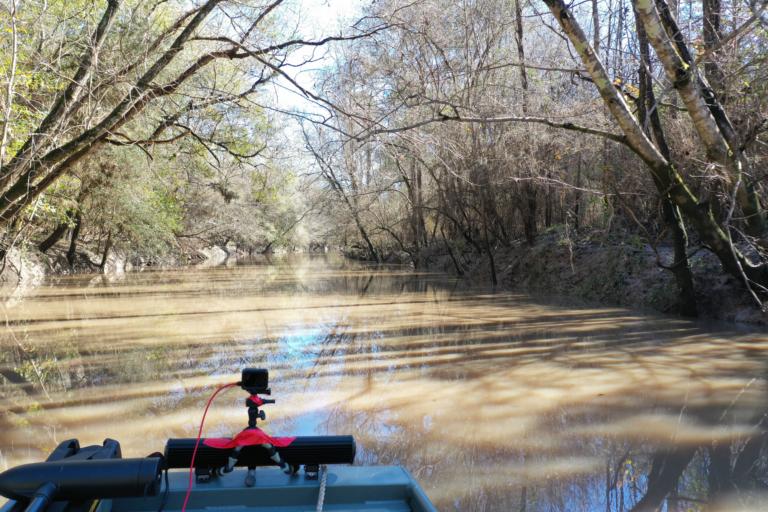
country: US
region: Louisiana
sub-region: Calcasieu Parish
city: Iowa
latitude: 30.3148
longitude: -93.0393
